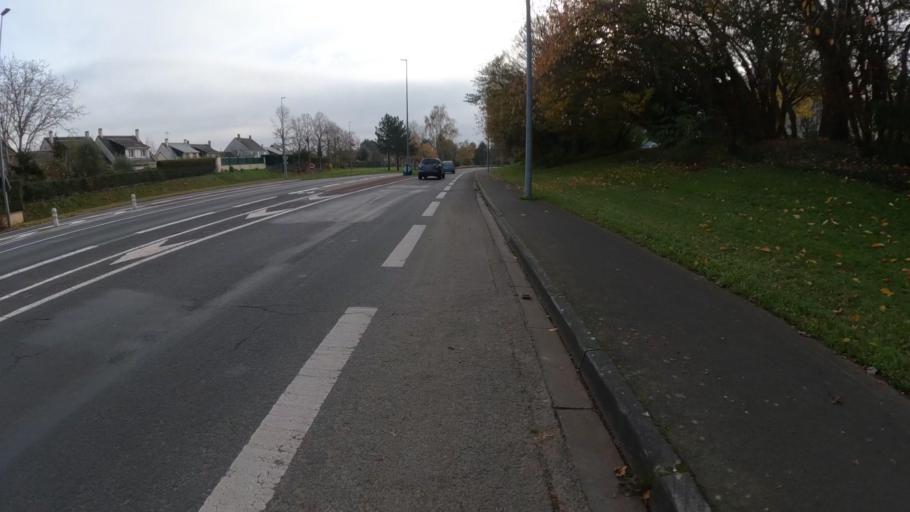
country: FR
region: Lower Normandy
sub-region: Departement du Calvados
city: Epron
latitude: 49.2043
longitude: -0.3755
